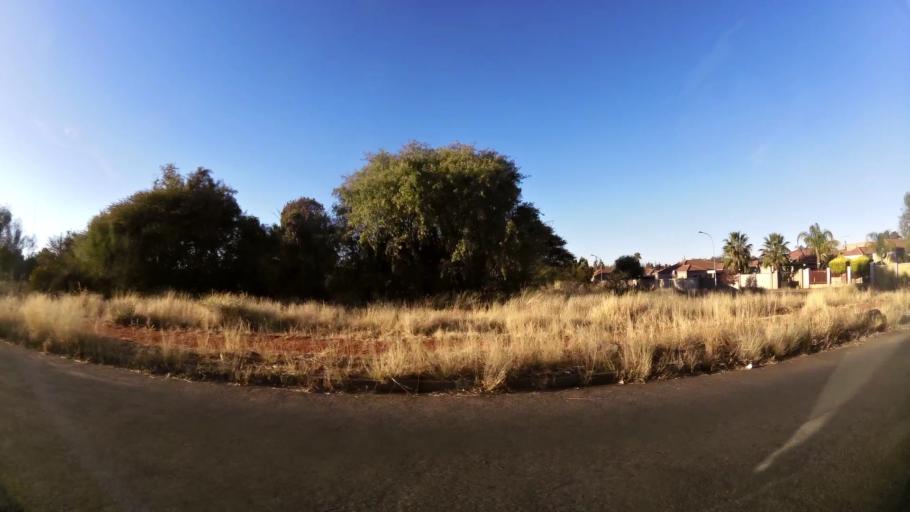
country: ZA
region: Northern Cape
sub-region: Frances Baard District Municipality
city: Kimberley
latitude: -28.7608
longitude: 24.7432
